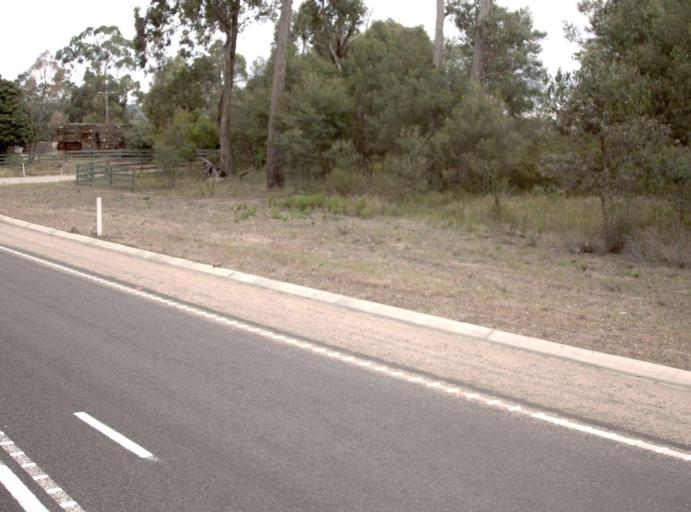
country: AU
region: Victoria
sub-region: East Gippsland
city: Lakes Entrance
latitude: -37.7244
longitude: 148.0868
